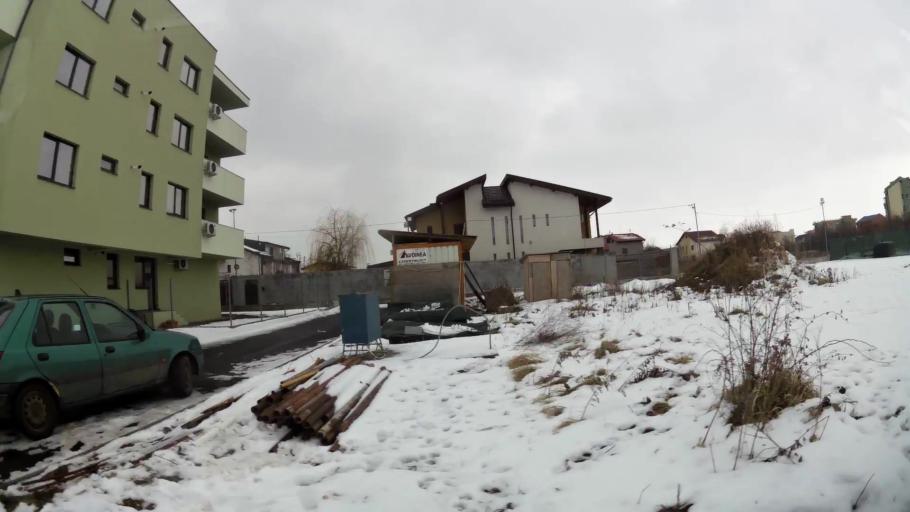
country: RO
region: Ilfov
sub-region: Comuna Otopeni
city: Otopeni
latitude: 44.5445
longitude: 26.0758
